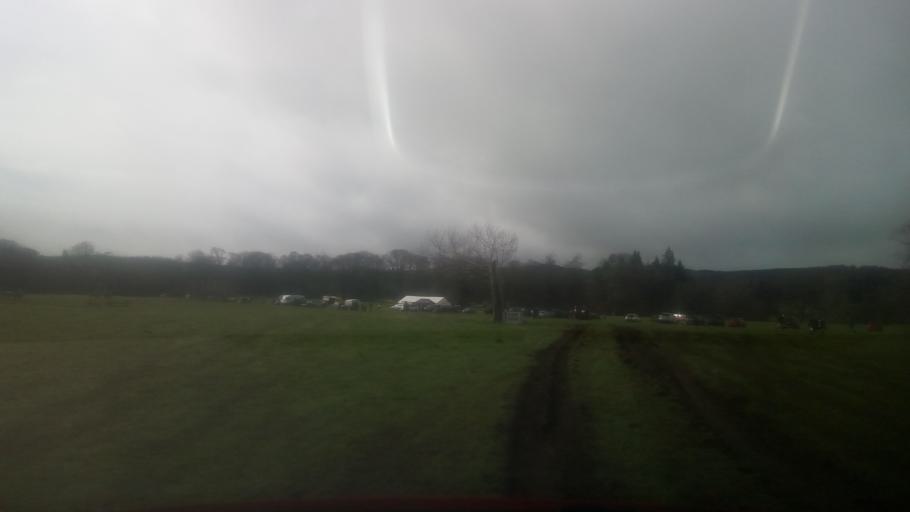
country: GB
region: Scotland
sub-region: The Scottish Borders
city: Duns
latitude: 55.7792
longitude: -2.3492
